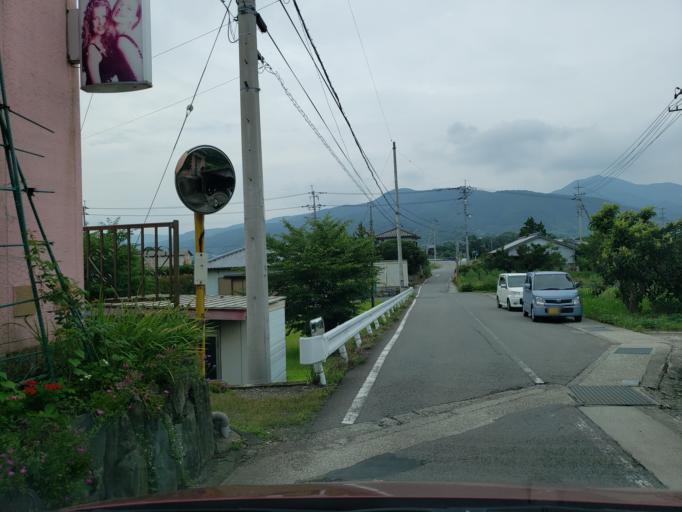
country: JP
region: Tokushima
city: Kamojimacho-jogejima
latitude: 34.1013
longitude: 134.2787
